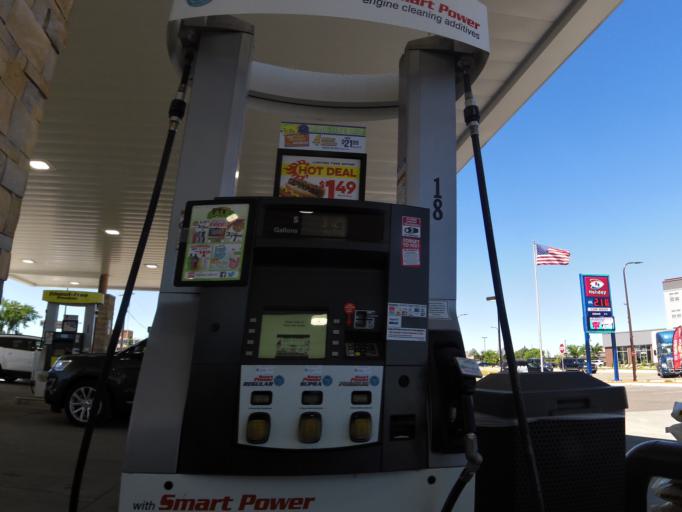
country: US
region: Minnesota
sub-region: Becker County
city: Detroit Lakes
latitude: 46.8154
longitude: -95.8406
